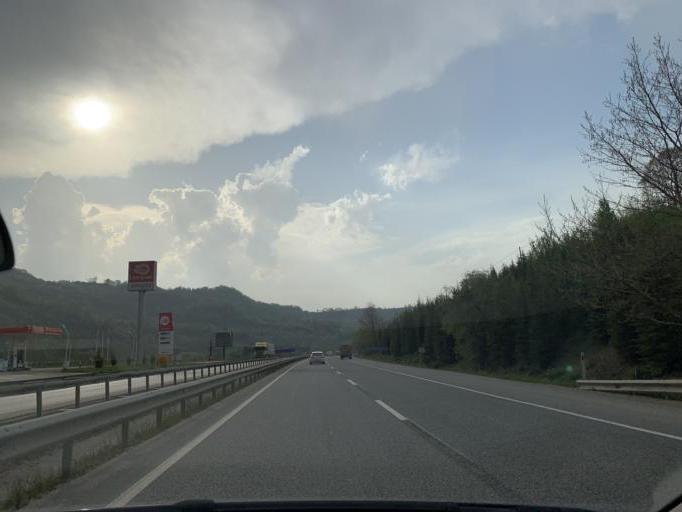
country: TR
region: Bursa
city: Tahtakopru
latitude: 39.9561
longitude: 29.6649
